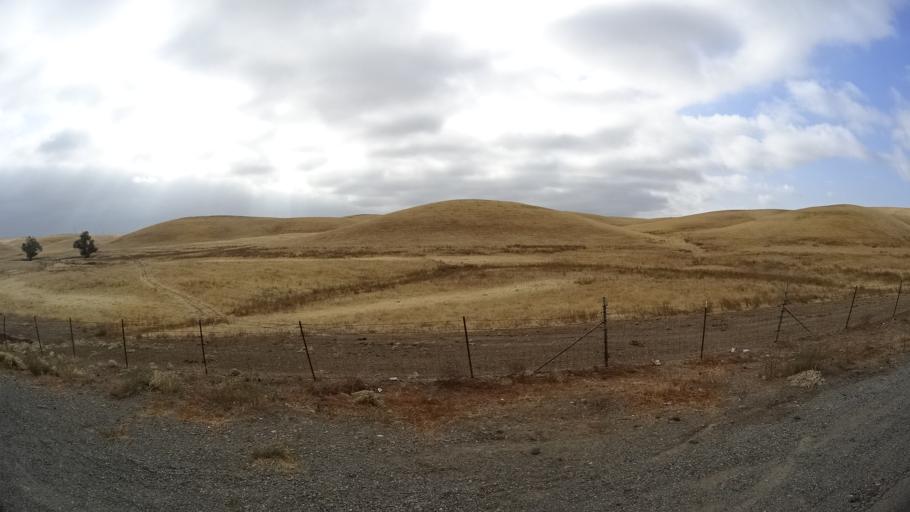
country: US
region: California
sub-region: Yolo County
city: Dunnigan
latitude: 38.7832
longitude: -121.9295
